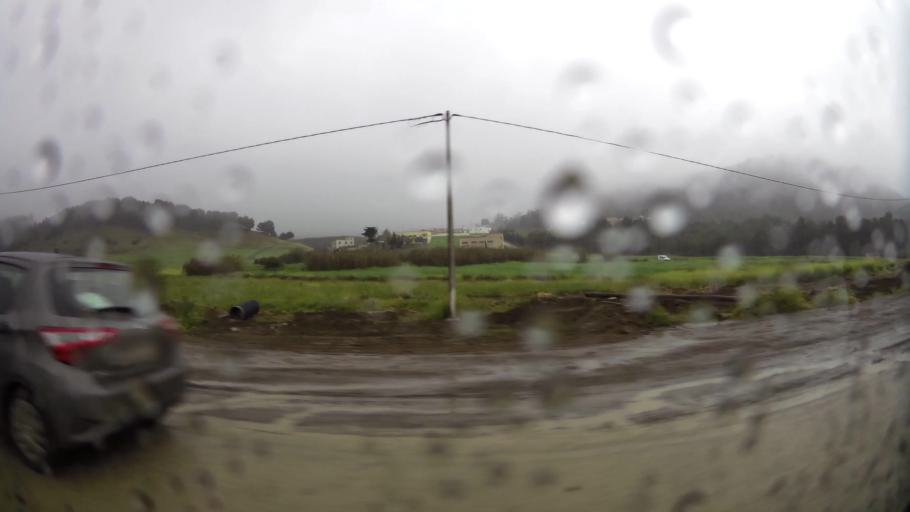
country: MA
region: Taza-Al Hoceima-Taounate
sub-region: Taza
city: Aknoul
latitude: 34.7582
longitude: -3.8020
